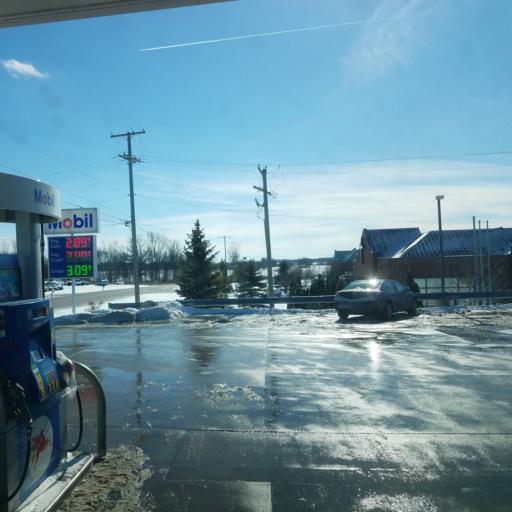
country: US
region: Michigan
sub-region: Livingston County
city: Fowlerville
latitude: 42.6446
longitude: -84.0735
